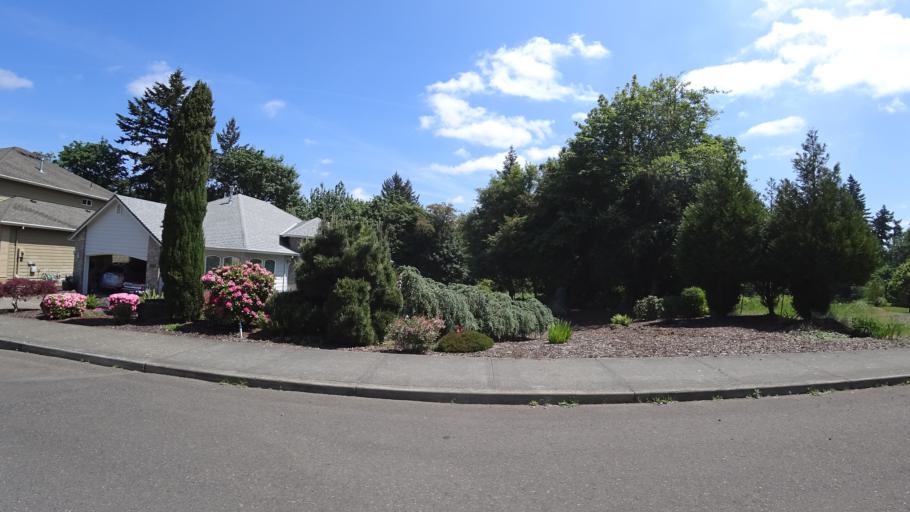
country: US
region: Oregon
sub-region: Clackamas County
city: Happy Valley
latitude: 45.4877
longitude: -122.4932
